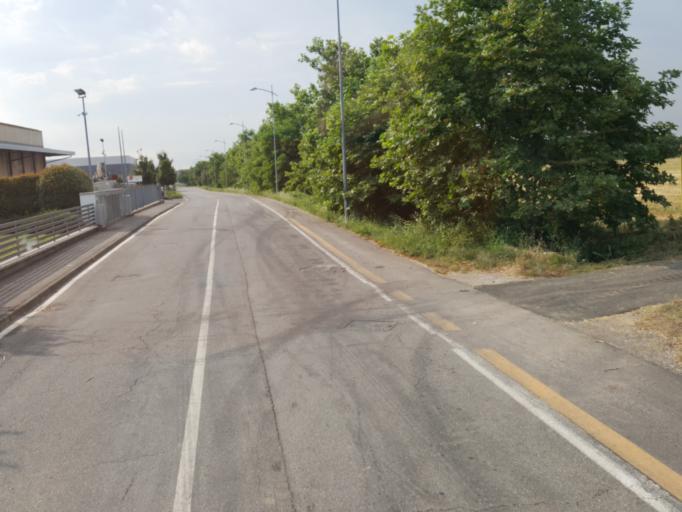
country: IT
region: Lombardy
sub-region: Provincia di Bergamo
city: Lallio
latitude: 45.6591
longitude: 9.6188
